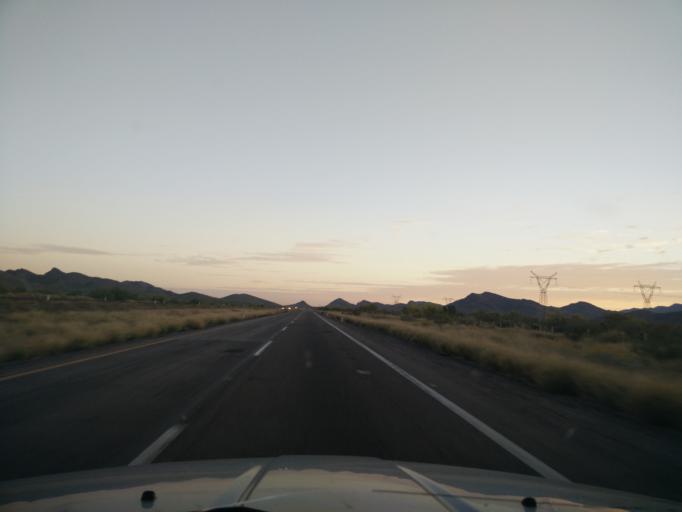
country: MX
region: Sonora
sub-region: Empalme
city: La Palma
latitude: 28.4095
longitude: -111.0438
